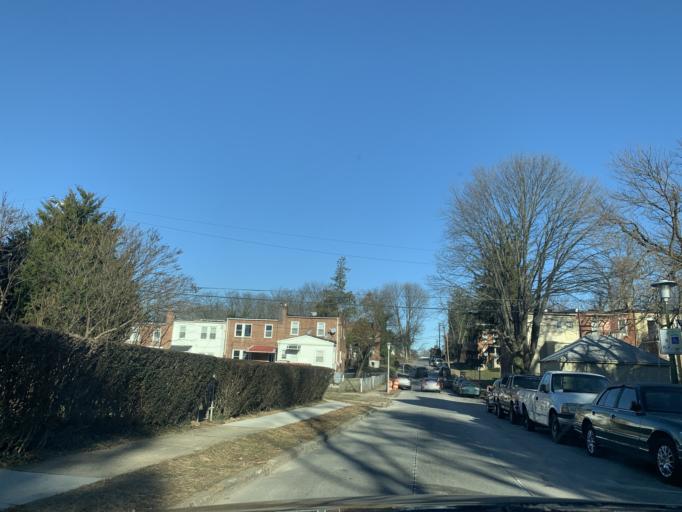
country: US
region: Maryland
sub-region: Baltimore County
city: Lochearn
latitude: 39.3205
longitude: -76.6849
